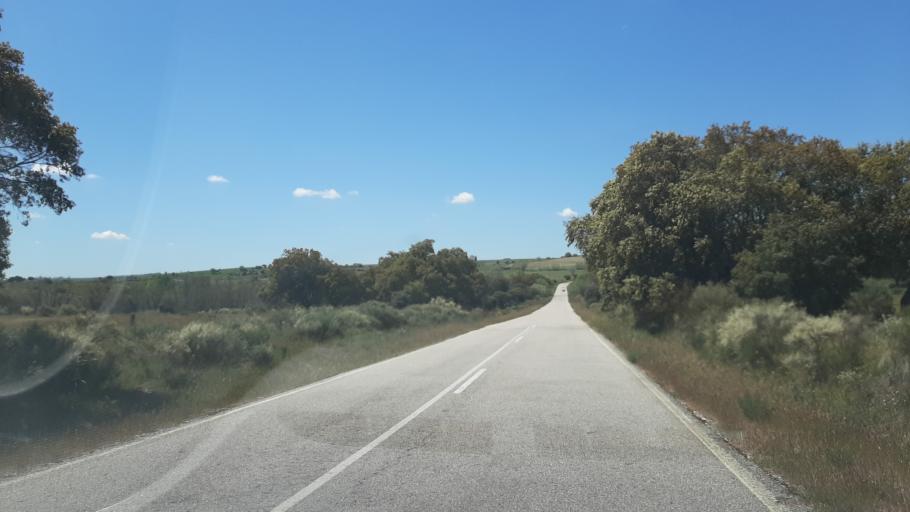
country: ES
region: Castille and Leon
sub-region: Provincia de Salamanca
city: Villarmuerto
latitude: 41.0344
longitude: -6.3975
